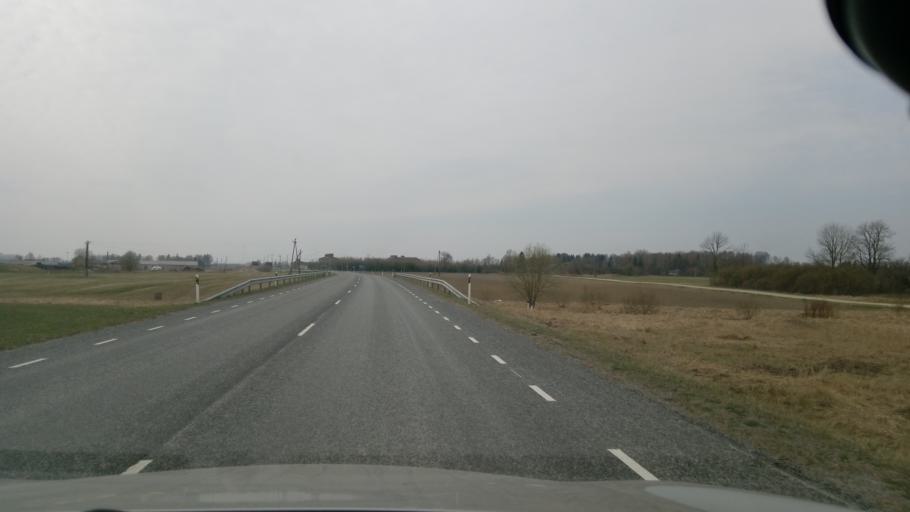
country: EE
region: Jaervamaa
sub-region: Tueri vald
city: Sarevere
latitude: 58.7791
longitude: 25.4903
